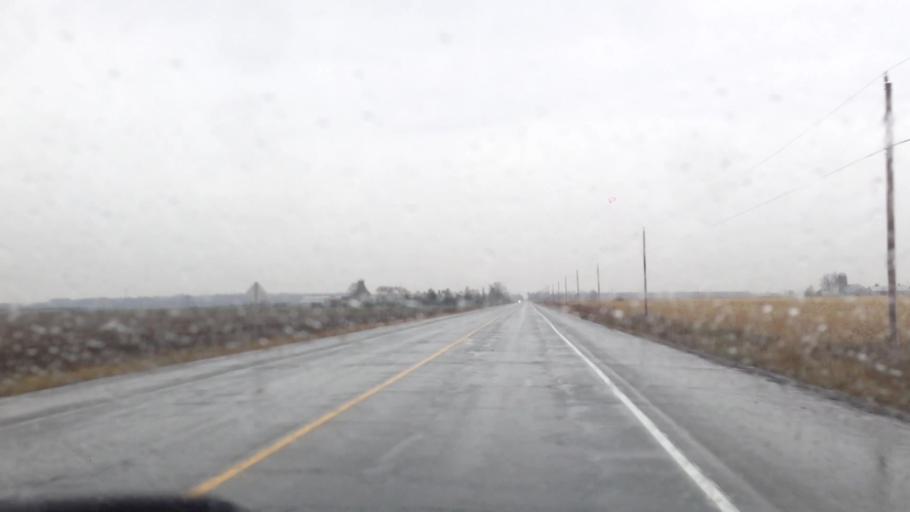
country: CA
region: Ontario
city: Clarence-Rockland
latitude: 45.4582
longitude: -75.4284
